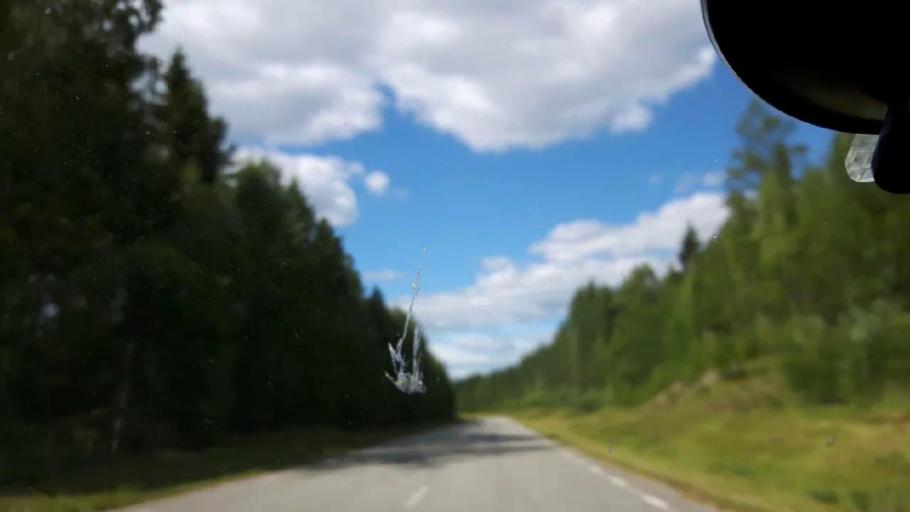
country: SE
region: Vaesternorrland
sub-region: Ange Kommun
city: Fransta
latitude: 62.7535
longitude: 16.3163
